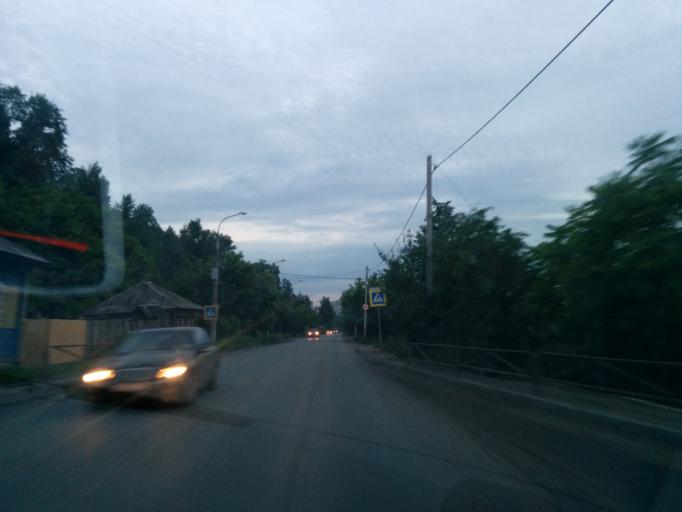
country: RU
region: Perm
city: Perm
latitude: 58.0453
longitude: 56.3216
